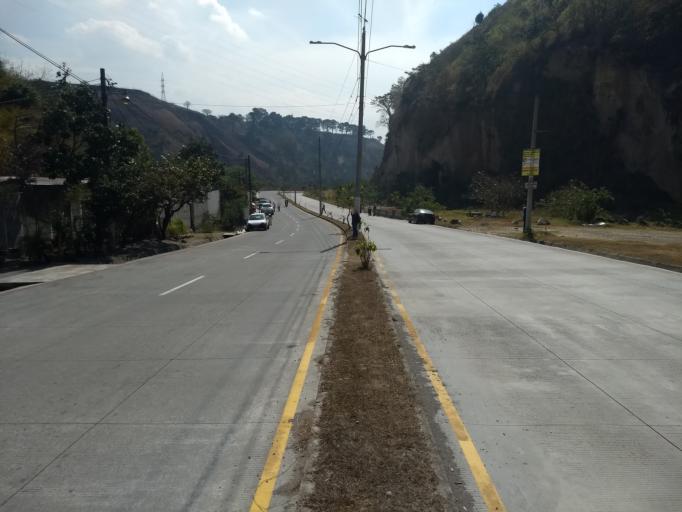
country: GT
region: Guatemala
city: Villa Nueva
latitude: 14.5526
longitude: -90.5915
